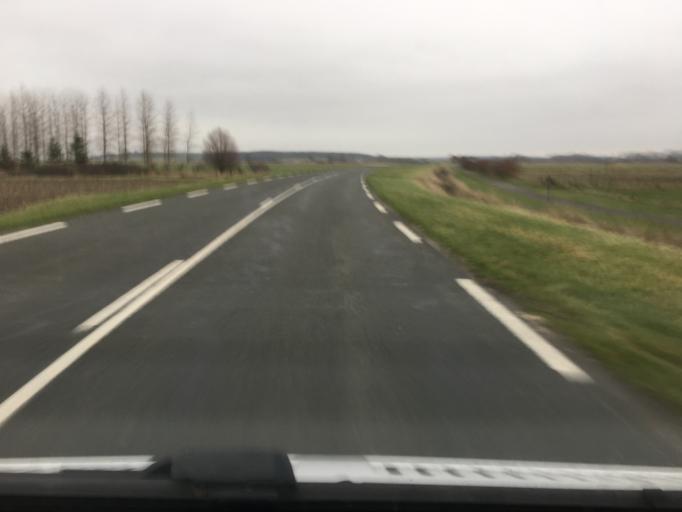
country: FR
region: Picardie
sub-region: Departement de la Somme
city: Pende
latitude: 50.1892
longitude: 1.5701
